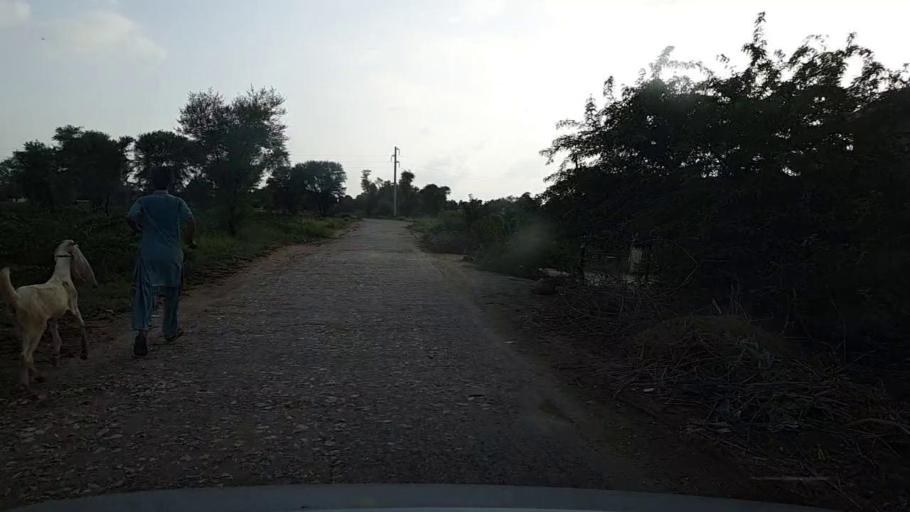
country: PK
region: Sindh
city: Pad Idan
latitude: 26.7925
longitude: 68.2244
